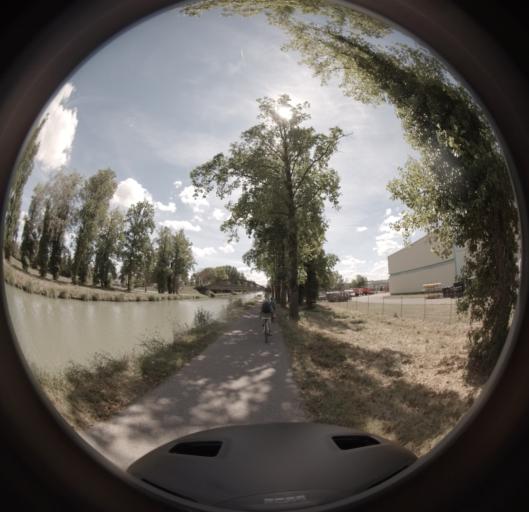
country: FR
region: Midi-Pyrenees
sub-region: Departement du Tarn-et-Garonne
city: Castelsarrasin
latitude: 44.0601
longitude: 1.1034
